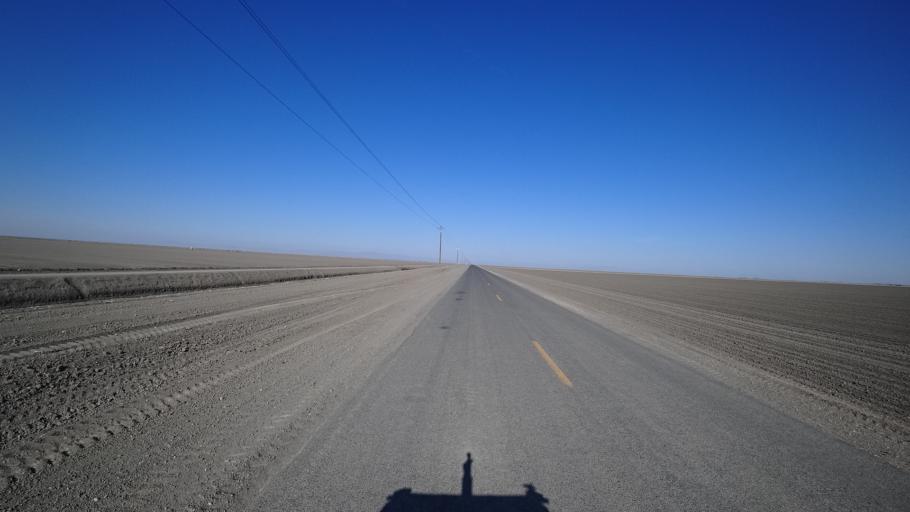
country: US
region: California
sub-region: Kings County
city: Corcoran
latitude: 36.0797
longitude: -119.7028
